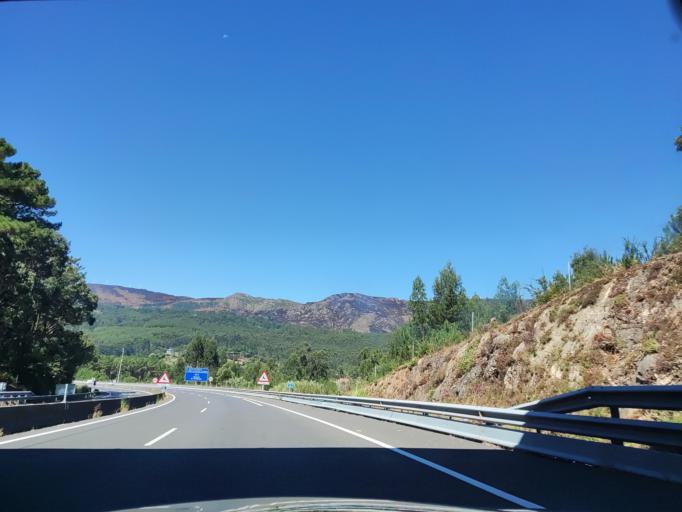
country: ES
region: Galicia
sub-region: Provincia da Coruna
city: Boiro
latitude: 42.6598
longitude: -8.8867
